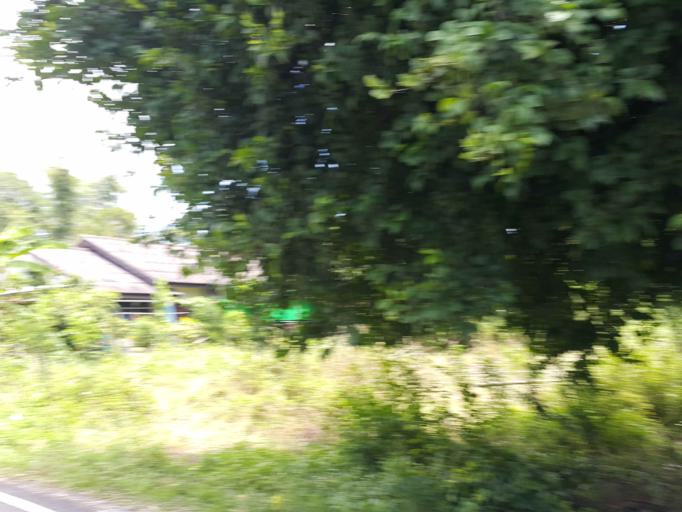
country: TH
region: Chiang Mai
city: San Sai
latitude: 18.8074
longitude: 99.0482
